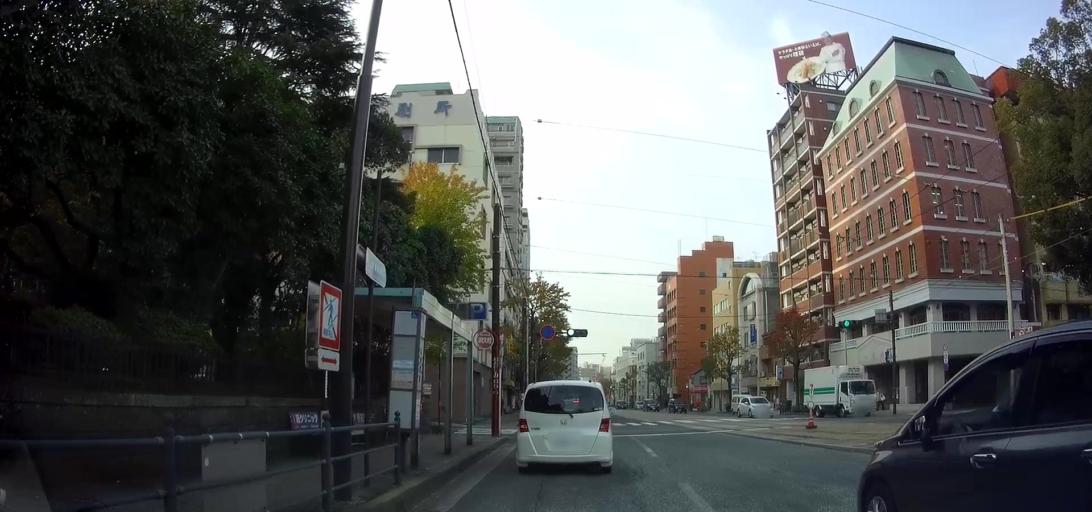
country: JP
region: Nagasaki
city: Nagasaki-shi
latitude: 32.7490
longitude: 129.8803
